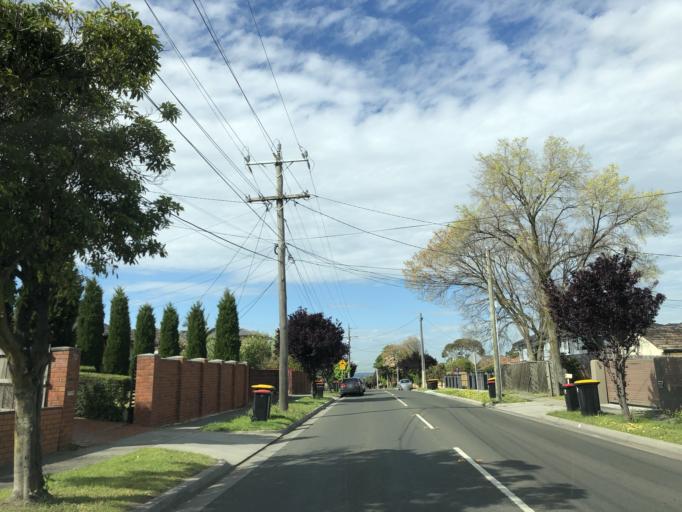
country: AU
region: Victoria
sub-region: Greater Dandenong
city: Dandenong
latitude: -37.9770
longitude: 145.2020
